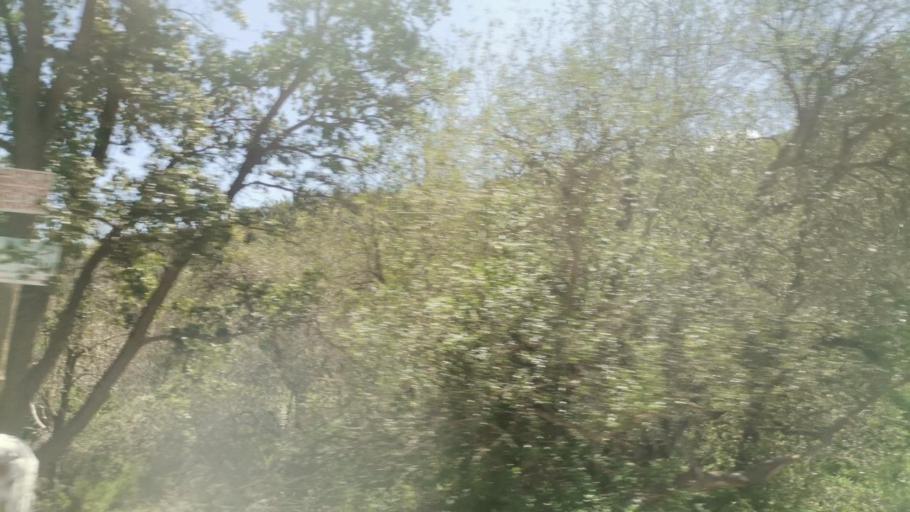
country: CL
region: Valparaiso
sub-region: Provincia de Marga Marga
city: Limache
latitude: -33.1930
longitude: -71.2803
